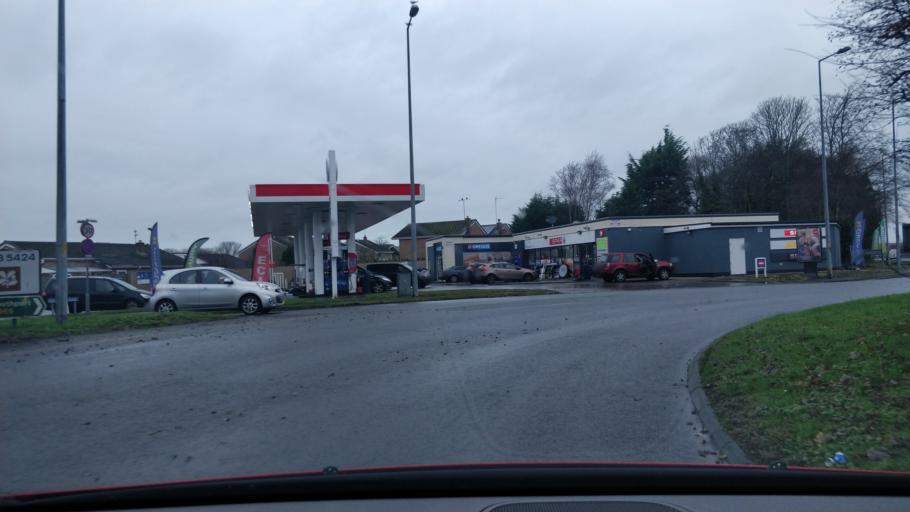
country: GB
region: England
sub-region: Sefton
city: Formby
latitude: 53.5684
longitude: -3.0479
